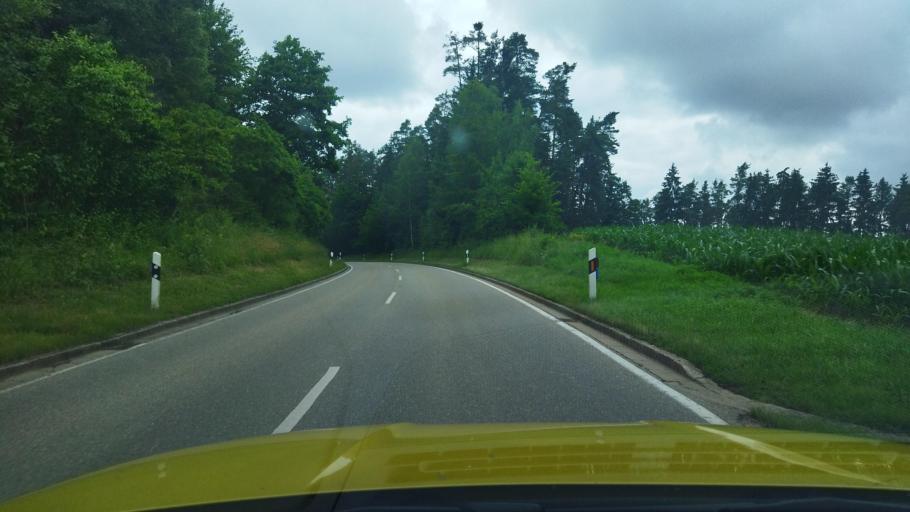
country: DE
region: Bavaria
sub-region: Regierungsbezirk Mittelfranken
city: Pleinfeld
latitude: 49.0943
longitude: 11.0005
